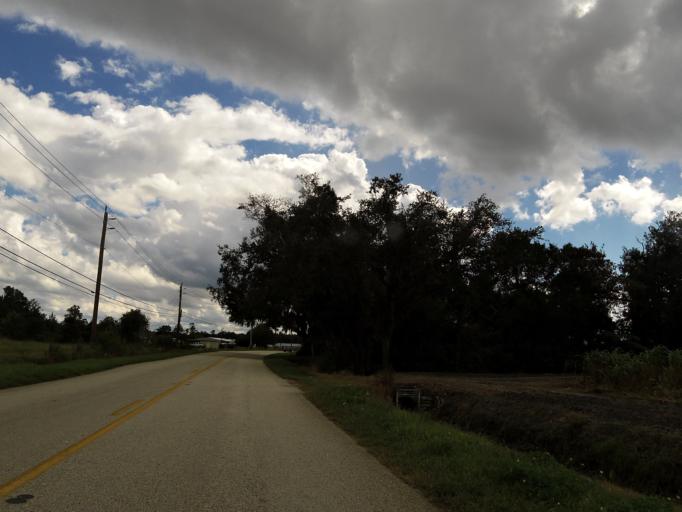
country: US
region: Florida
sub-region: Saint Johns County
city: Saint Augustine South
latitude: 29.8471
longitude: -81.4987
